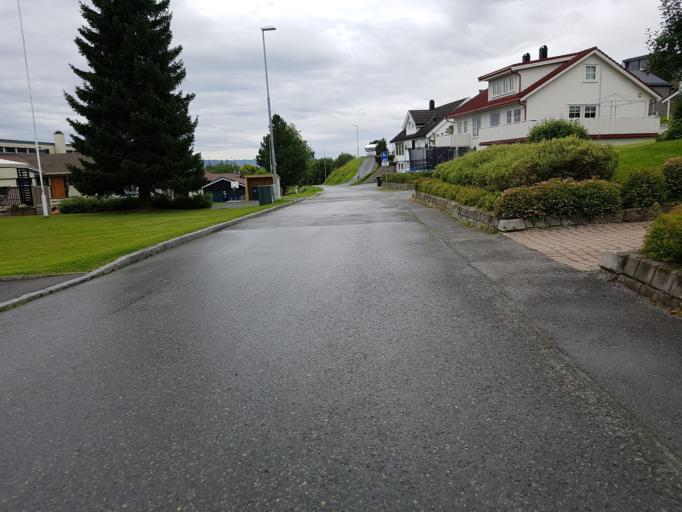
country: NO
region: Sor-Trondelag
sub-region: Trondheim
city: Trondheim
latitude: 63.3868
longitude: 10.3365
